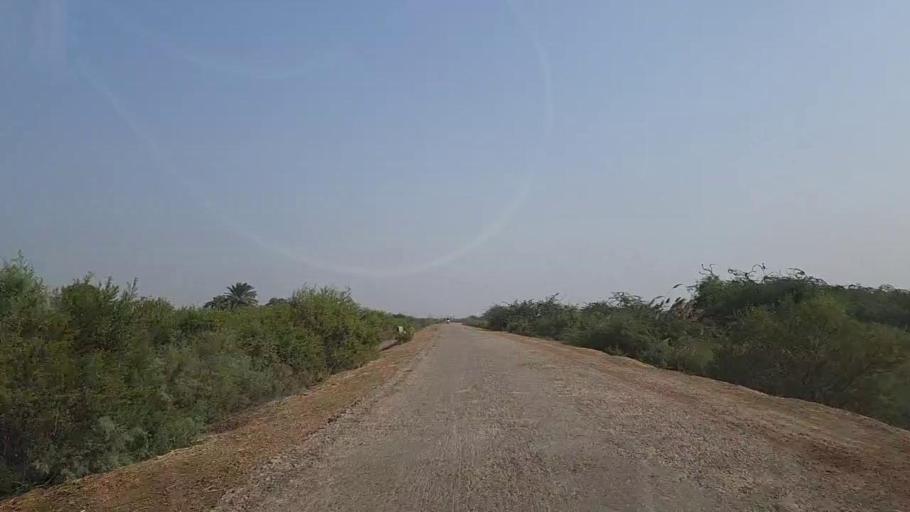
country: PK
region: Sindh
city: Keti Bandar
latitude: 24.2292
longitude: 67.6612
